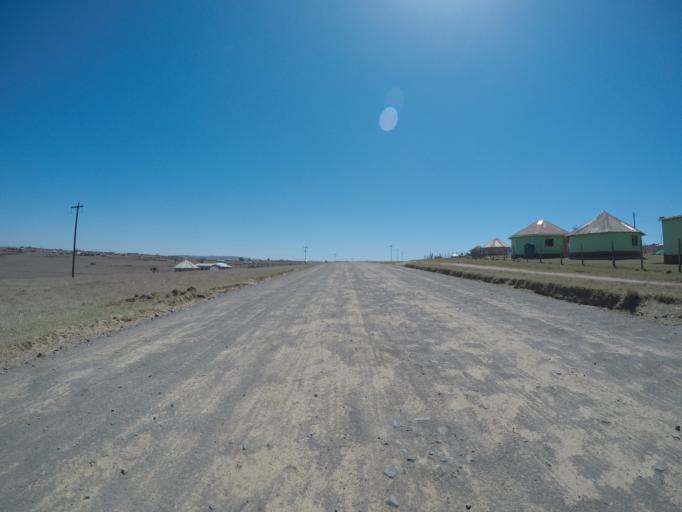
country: ZA
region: Eastern Cape
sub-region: OR Tambo District Municipality
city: Mthatha
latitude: -31.7873
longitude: 28.8143
